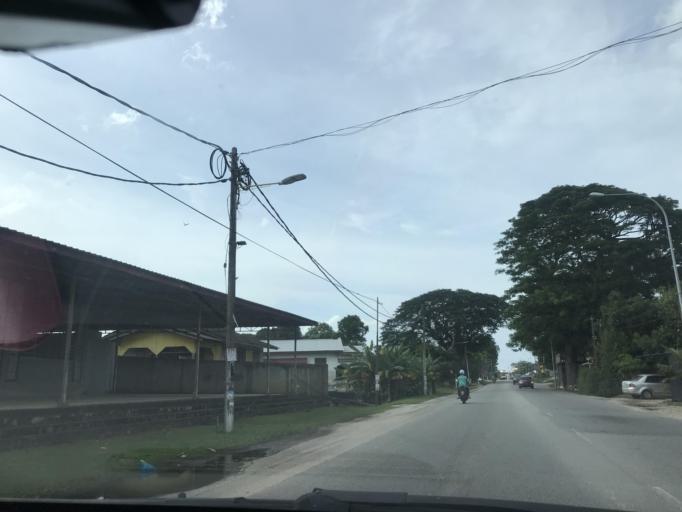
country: MY
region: Kelantan
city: Kota Bharu
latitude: 6.1054
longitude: 102.2357
